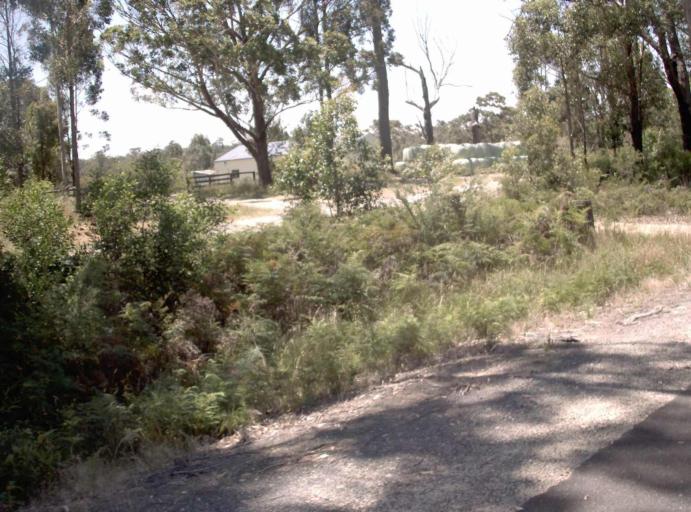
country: AU
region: Victoria
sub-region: East Gippsland
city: Lakes Entrance
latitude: -37.7517
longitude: 148.2912
